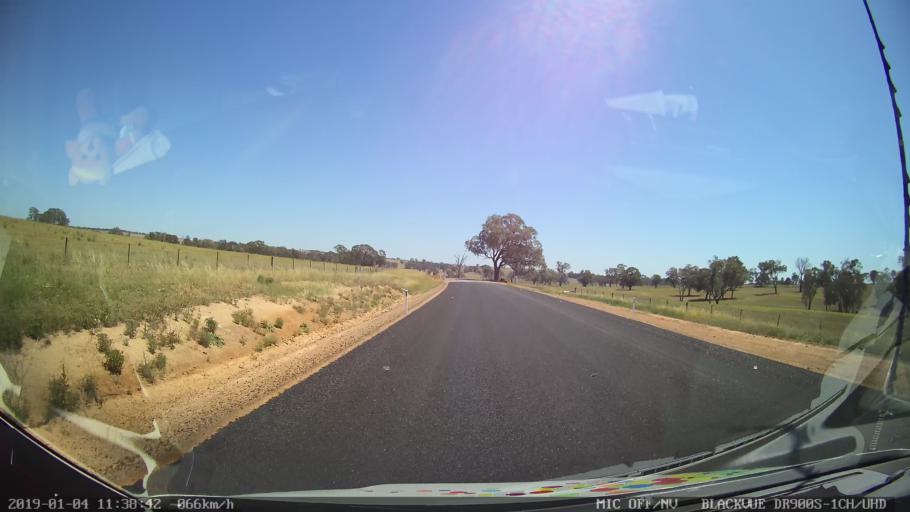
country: AU
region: New South Wales
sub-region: Cabonne
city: Molong
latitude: -33.0202
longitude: 148.8012
